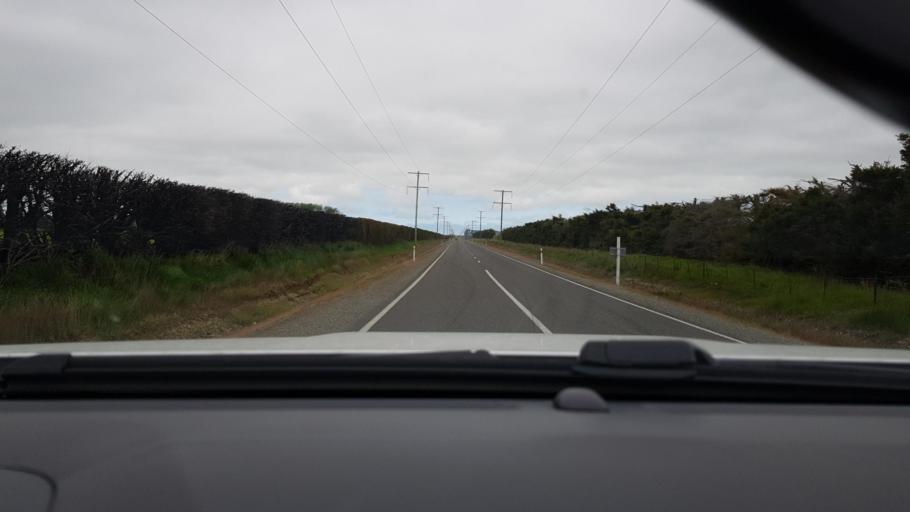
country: NZ
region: Otago
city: Oamaru
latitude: -44.9646
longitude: 171.0231
